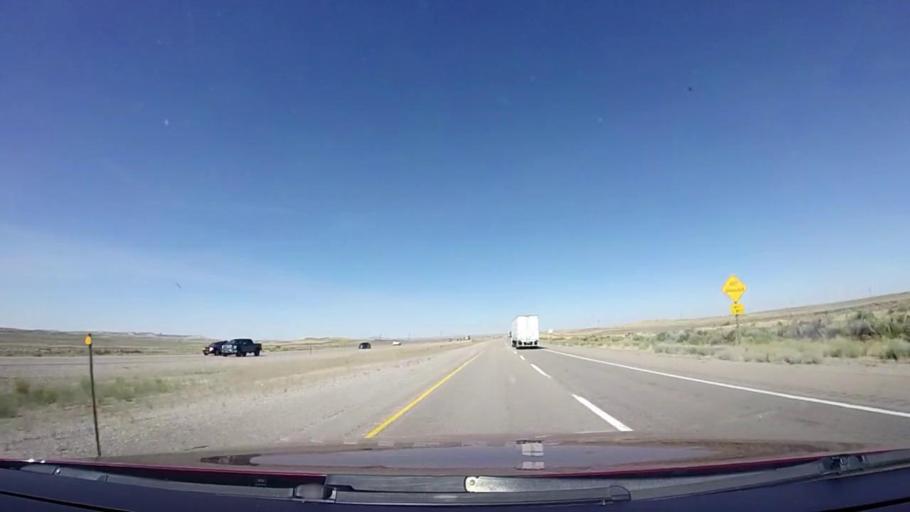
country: US
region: Wyoming
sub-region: Sweetwater County
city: Rock Springs
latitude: 41.6324
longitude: -108.3592
